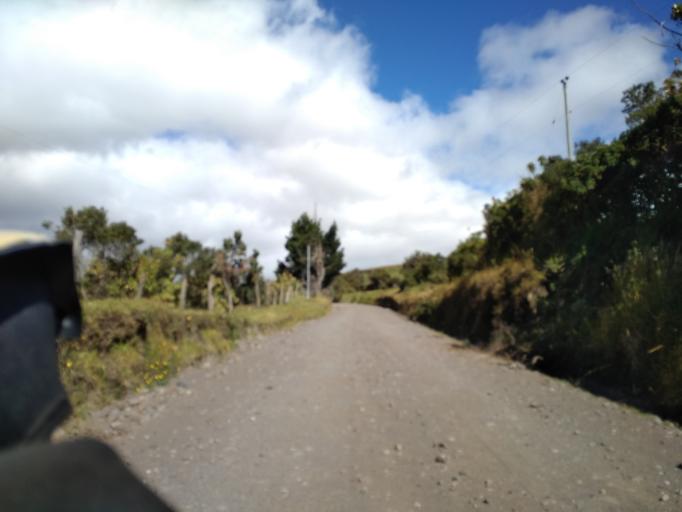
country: EC
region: Pichincha
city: Machachi
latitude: -0.5361
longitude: -78.4775
